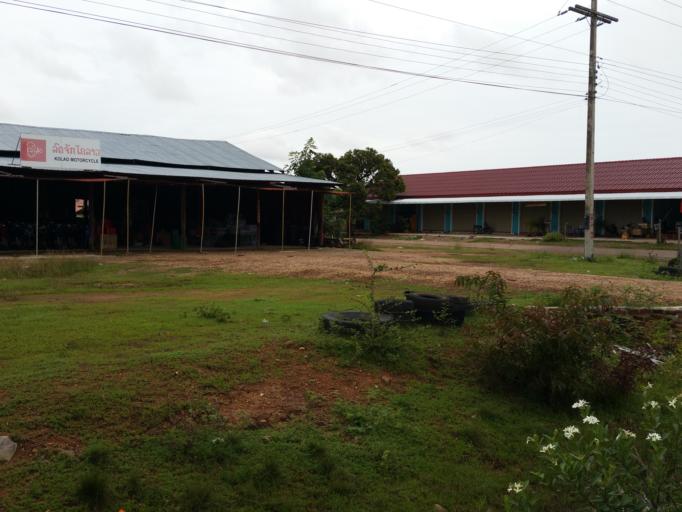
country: LA
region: Champasak
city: Khong
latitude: 14.0890
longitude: 105.8823
